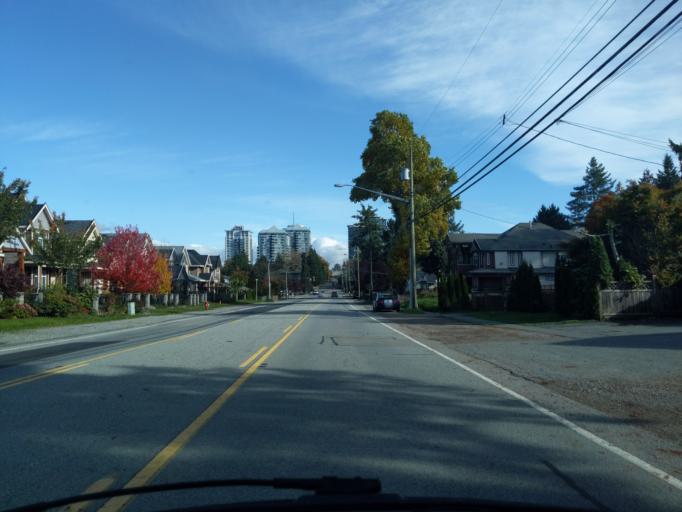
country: CA
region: British Columbia
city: New Westminster
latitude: 49.1989
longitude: -122.8595
